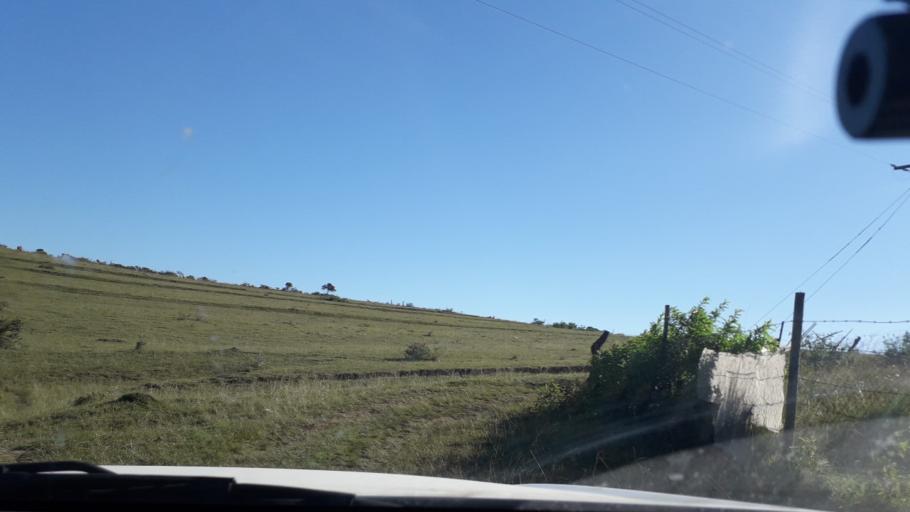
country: ZA
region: Eastern Cape
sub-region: Buffalo City Metropolitan Municipality
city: East London
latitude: -32.8426
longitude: 27.9850
